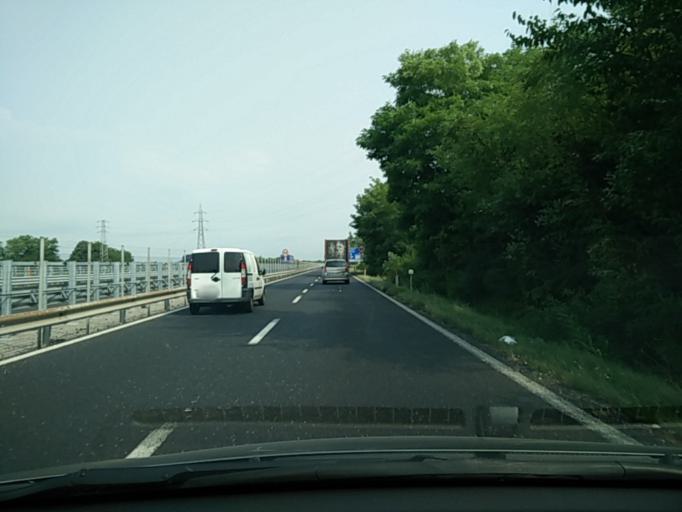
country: IT
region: Friuli Venezia Giulia
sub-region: Provincia di Udine
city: Pasian di Prato
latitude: 46.0538
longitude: 13.2025
